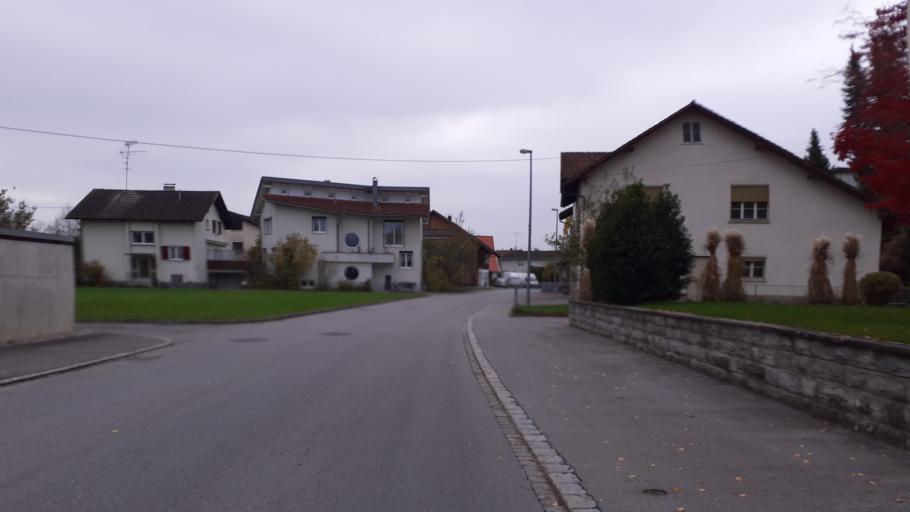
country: AT
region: Vorarlberg
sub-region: Politischer Bezirk Dornbirn
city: Lustenau
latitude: 47.4275
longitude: 9.6543
